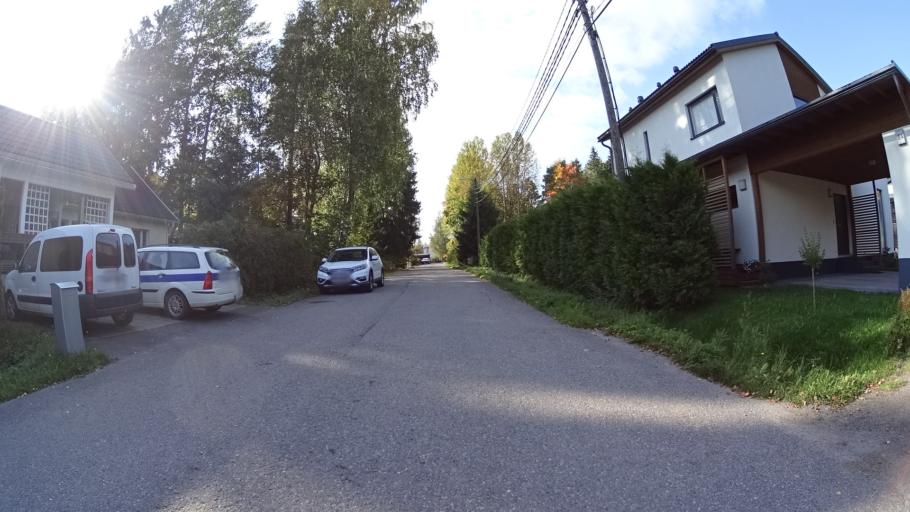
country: FI
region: Uusimaa
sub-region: Helsinki
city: Kilo
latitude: 60.2352
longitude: 24.8185
